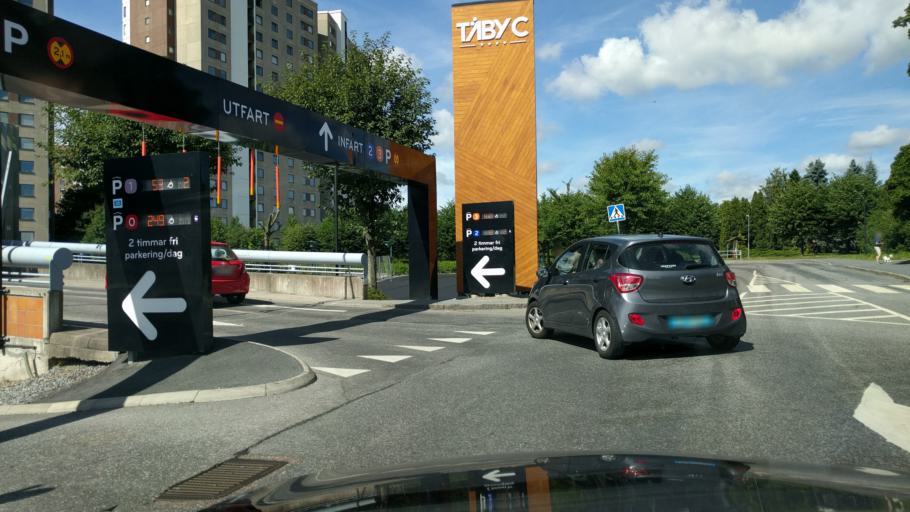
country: SE
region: Stockholm
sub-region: Taby Kommun
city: Taby
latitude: 59.4464
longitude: 18.0739
